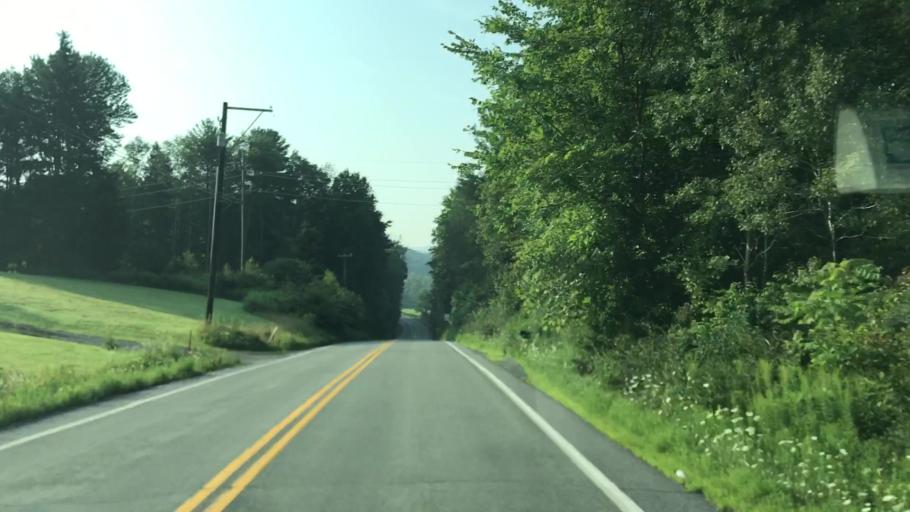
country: US
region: Pennsylvania
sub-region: Lackawanna County
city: Dalton
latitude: 41.5958
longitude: -75.6627
